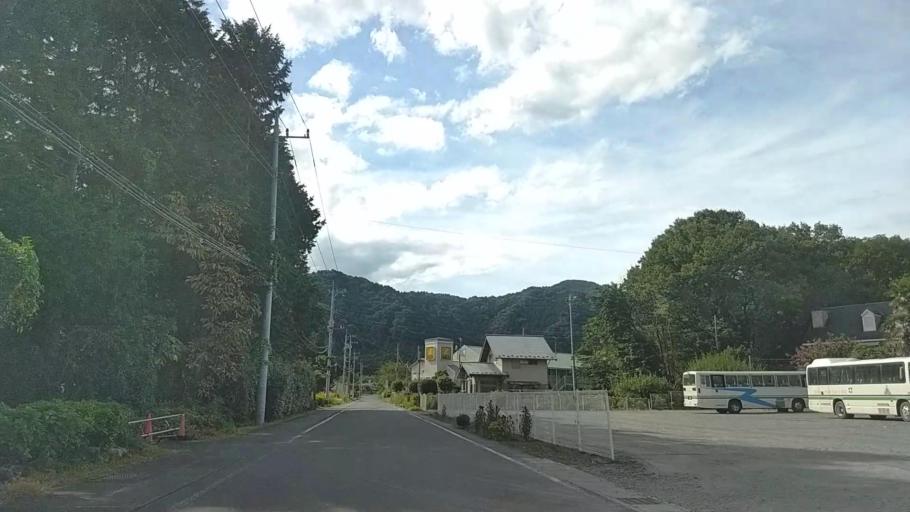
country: JP
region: Tochigi
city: Imaichi
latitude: 36.7804
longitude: 139.7035
